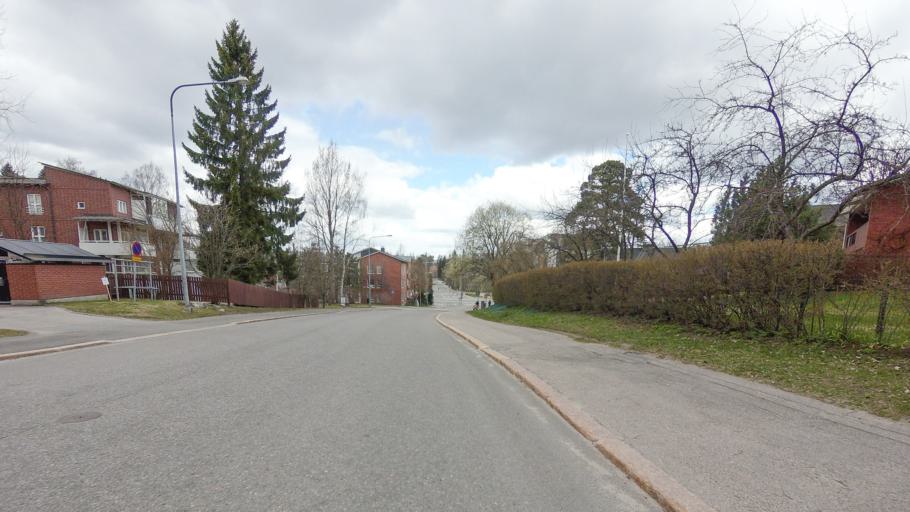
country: FI
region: Uusimaa
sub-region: Helsinki
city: Vantaa
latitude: 60.2171
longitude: 25.1047
